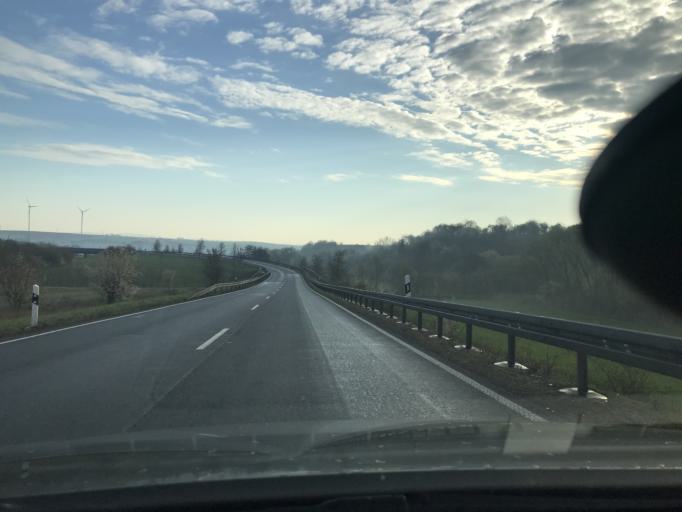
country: DE
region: Thuringia
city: Wipperdorf
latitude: 51.4378
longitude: 10.6456
